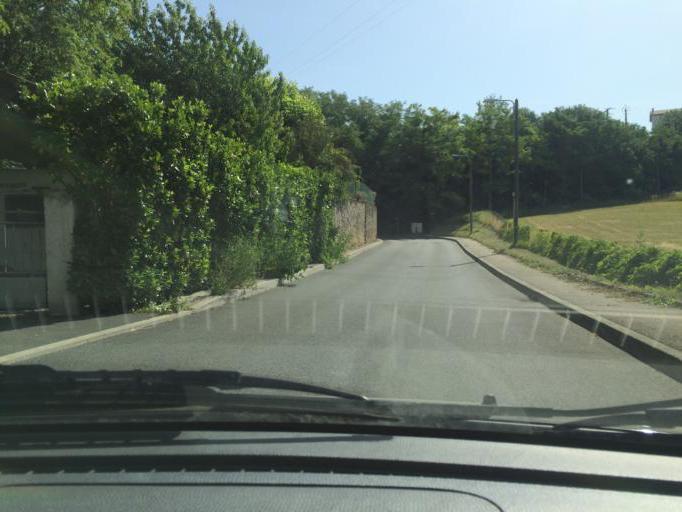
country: FR
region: Rhone-Alpes
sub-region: Departement du Rhone
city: Limonest
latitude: 45.8232
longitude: 4.7766
